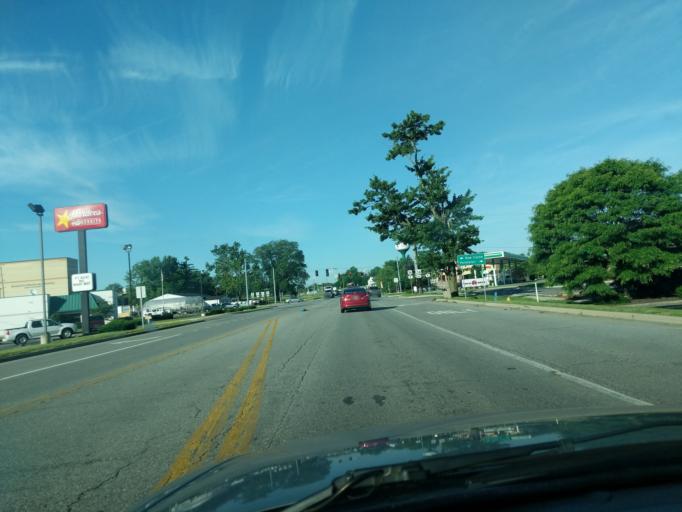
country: US
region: Indiana
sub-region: Madison County
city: Pendleton
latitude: 40.0008
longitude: -85.7340
